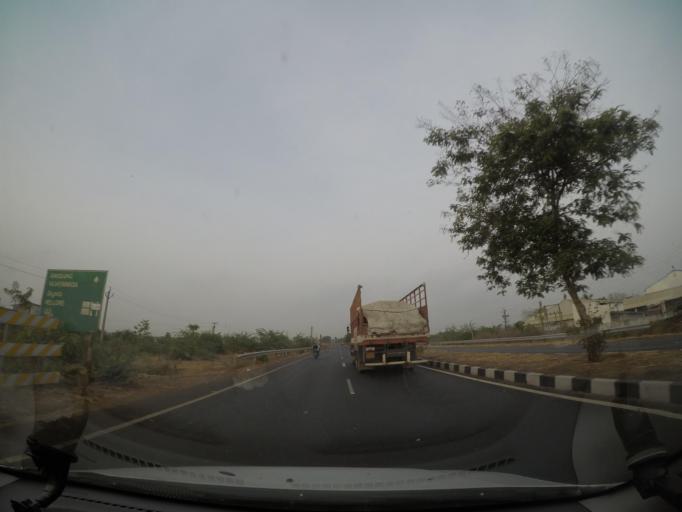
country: IN
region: Andhra Pradesh
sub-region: Krishna
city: Gannavaram
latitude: 16.6014
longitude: 80.8979
